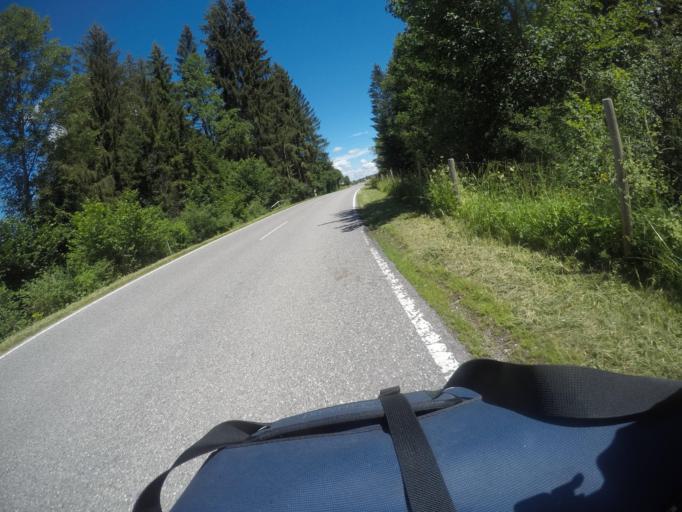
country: DE
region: Bavaria
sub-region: Upper Bavaria
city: Prem
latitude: 47.6627
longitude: 10.7847
